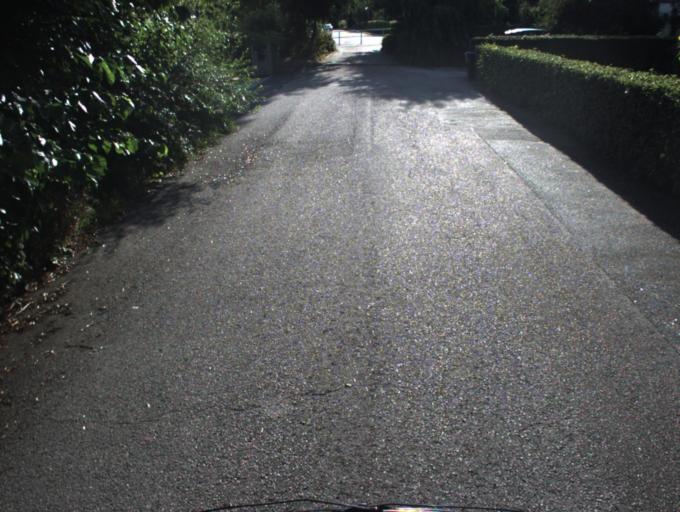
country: SE
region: Skane
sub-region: Helsingborg
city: Helsingborg
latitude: 56.0245
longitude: 12.7462
